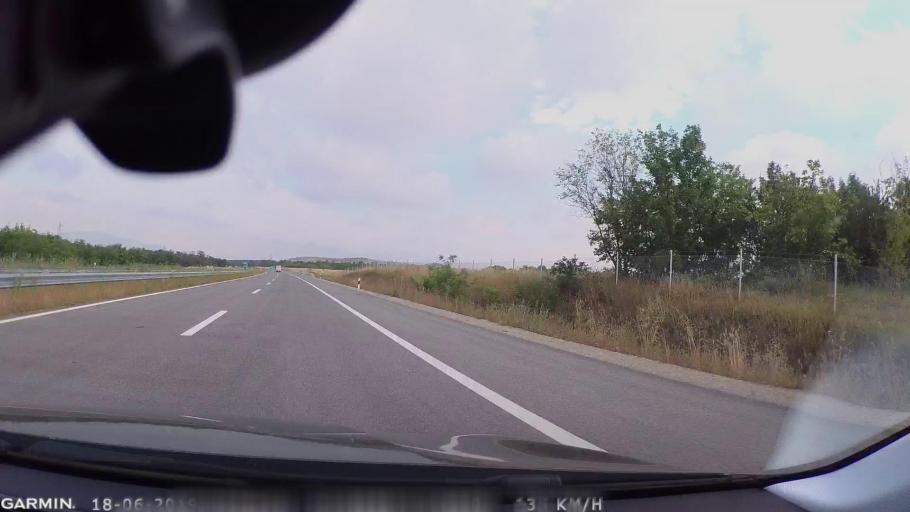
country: MK
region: Sveti Nikole
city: Sveti Nikole
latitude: 41.8400
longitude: 21.9825
